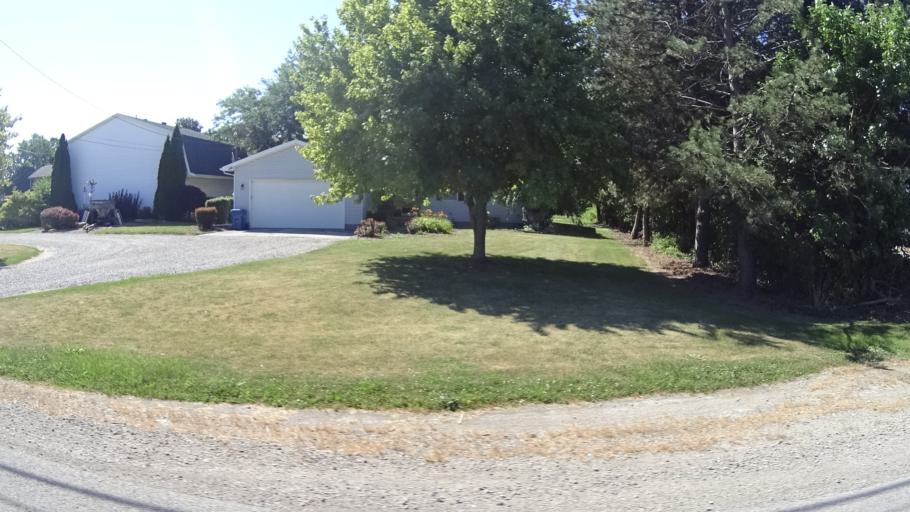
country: US
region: Ohio
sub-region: Erie County
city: Sandusky
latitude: 41.4088
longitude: -82.6989
